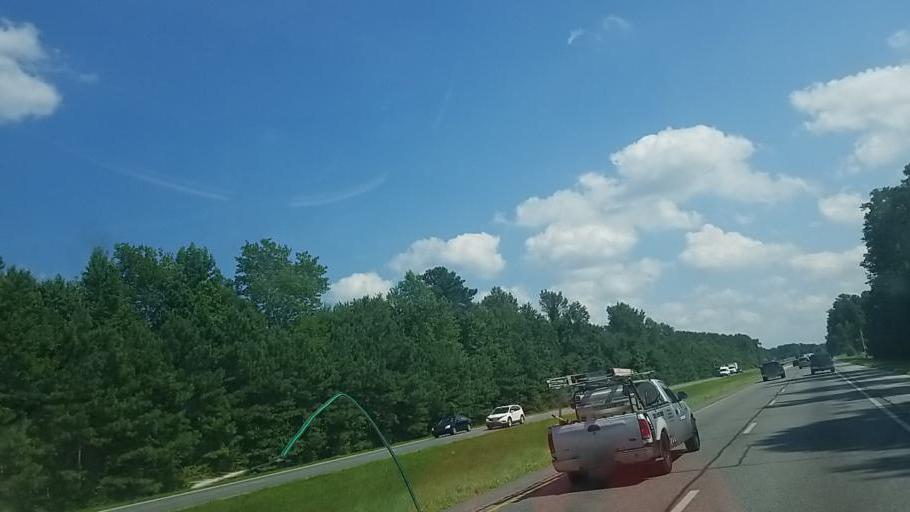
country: US
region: Delaware
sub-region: Sussex County
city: Georgetown
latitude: 38.7312
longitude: -75.4178
